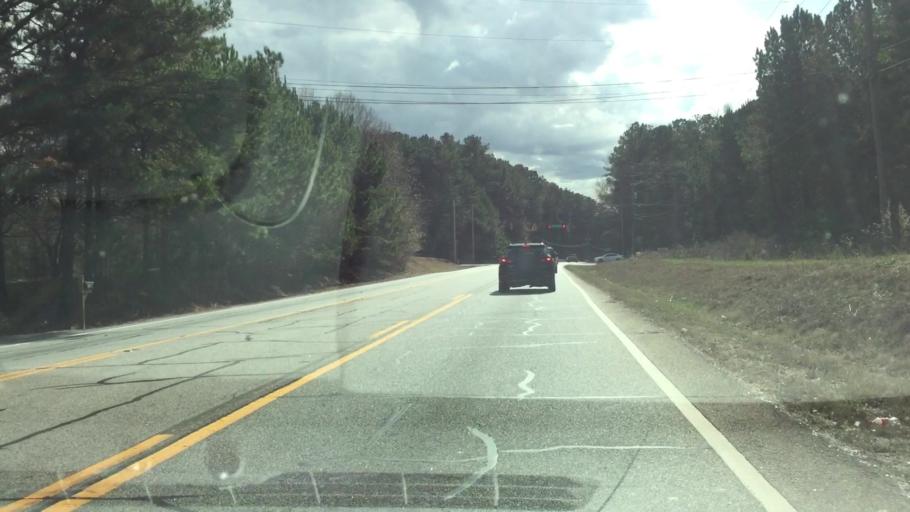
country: US
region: Georgia
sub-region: Henry County
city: McDonough
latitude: 33.4925
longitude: -84.1445
